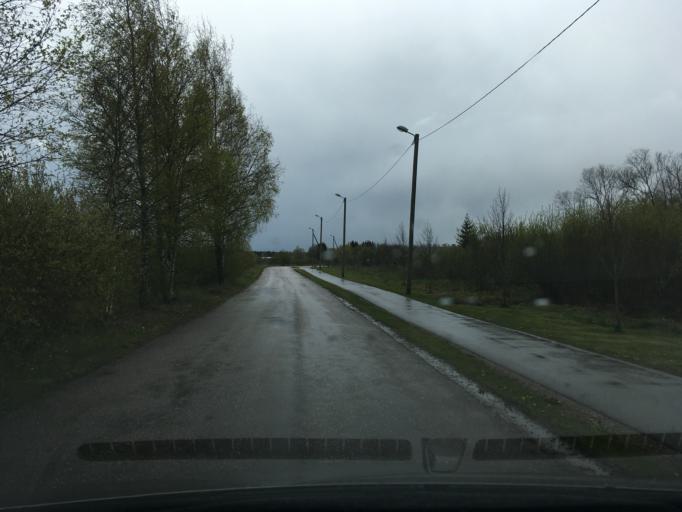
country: EE
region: Harju
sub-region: Joelaehtme vald
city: Loo
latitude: 59.4379
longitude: 24.9597
